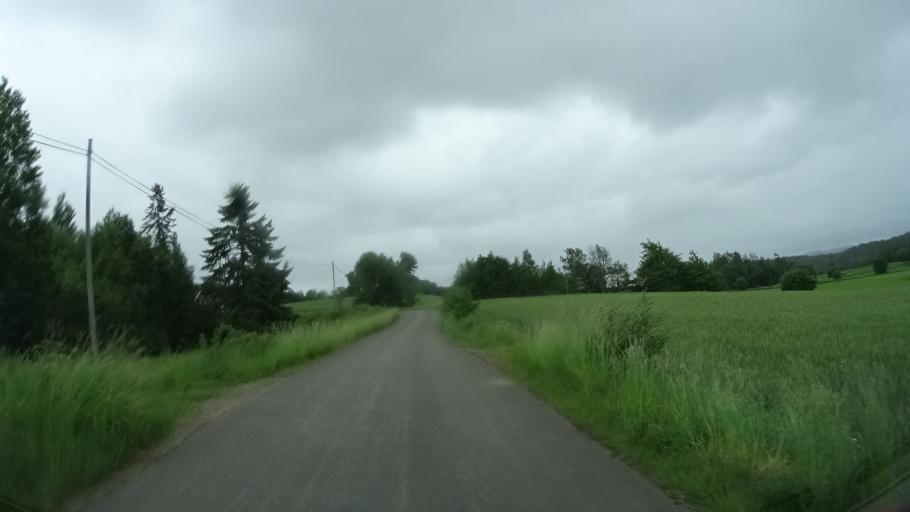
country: SE
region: Joenkoeping
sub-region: Eksjo Kommun
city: Mariannelund
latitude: 57.6826
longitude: 15.5757
